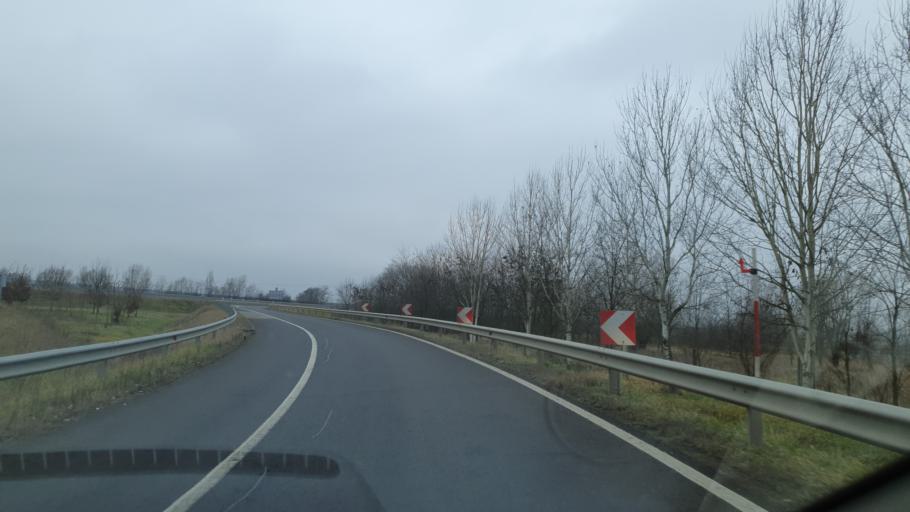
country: HU
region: Szabolcs-Szatmar-Bereg
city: Nyiregyhaza
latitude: 47.8848
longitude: 21.7080
